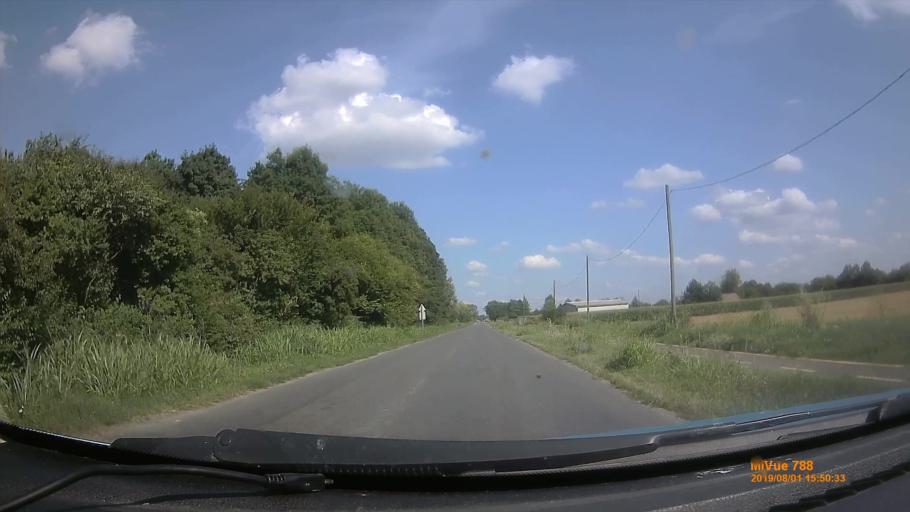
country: HU
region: Baranya
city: Szentlorinc
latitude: 46.0368
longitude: 18.0009
